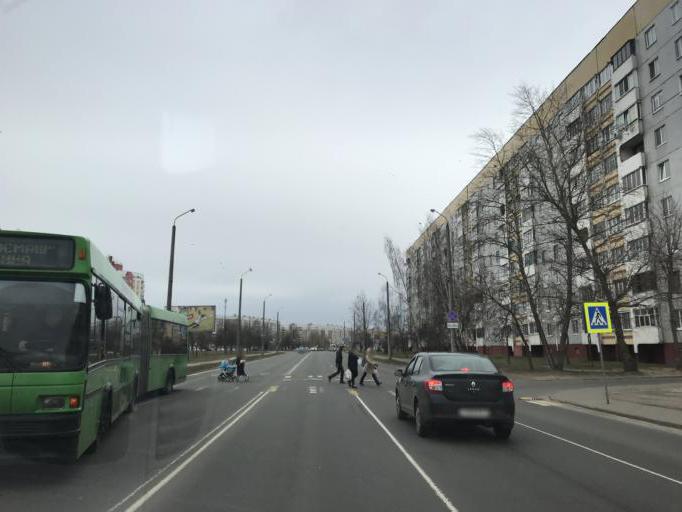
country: BY
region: Mogilev
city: Mahilyow
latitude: 53.8808
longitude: 30.3735
